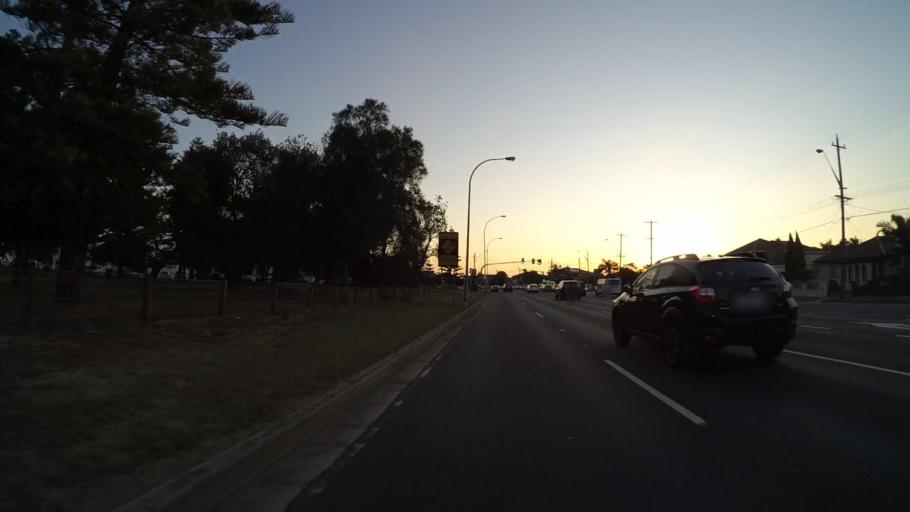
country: AU
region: New South Wales
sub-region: Rockdale
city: Brighton-Le-Sands
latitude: -33.9511
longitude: 151.1622
